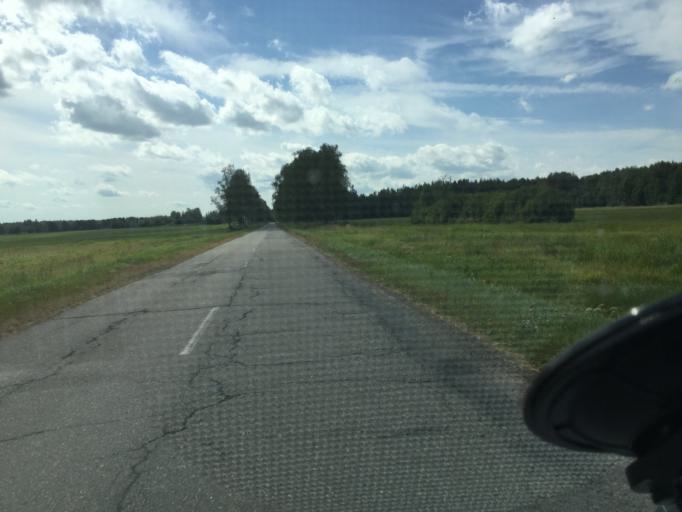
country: BY
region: Vitebsk
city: Chashniki
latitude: 55.3082
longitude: 29.4033
